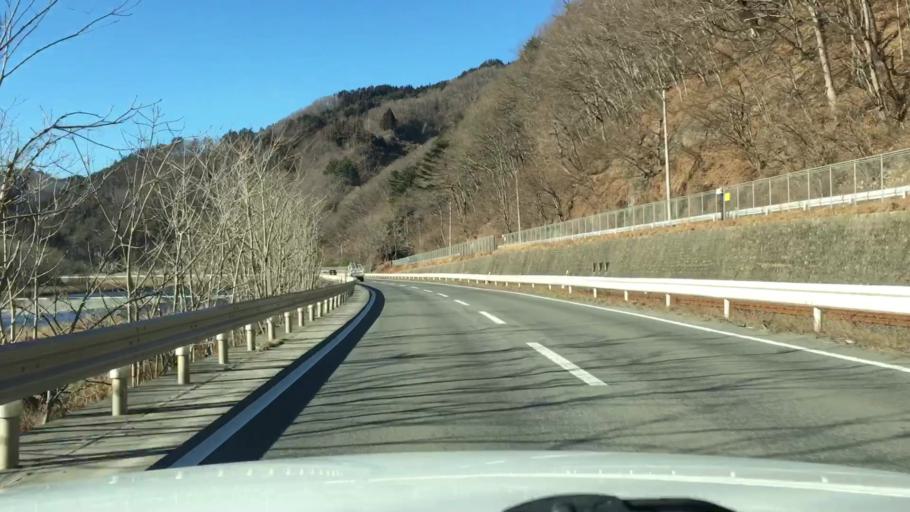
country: JP
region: Iwate
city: Miyako
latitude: 39.6326
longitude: 141.8524
